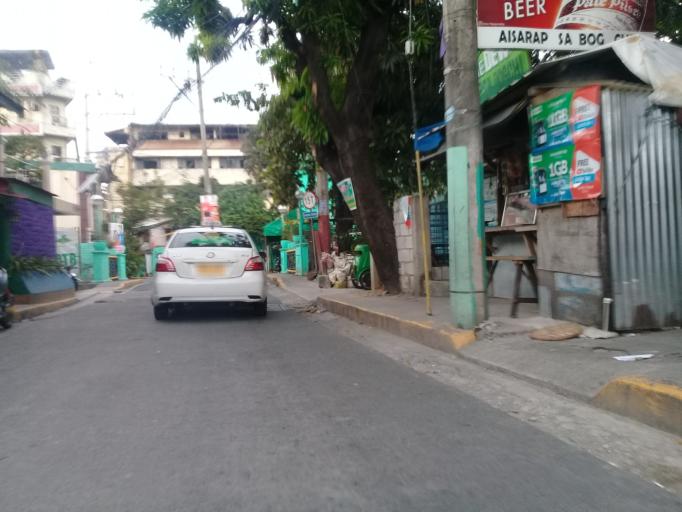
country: PH
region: Metro Manila
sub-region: Mandaluyong
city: Mandaluyong City
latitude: 14.5791
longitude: 121.0160
